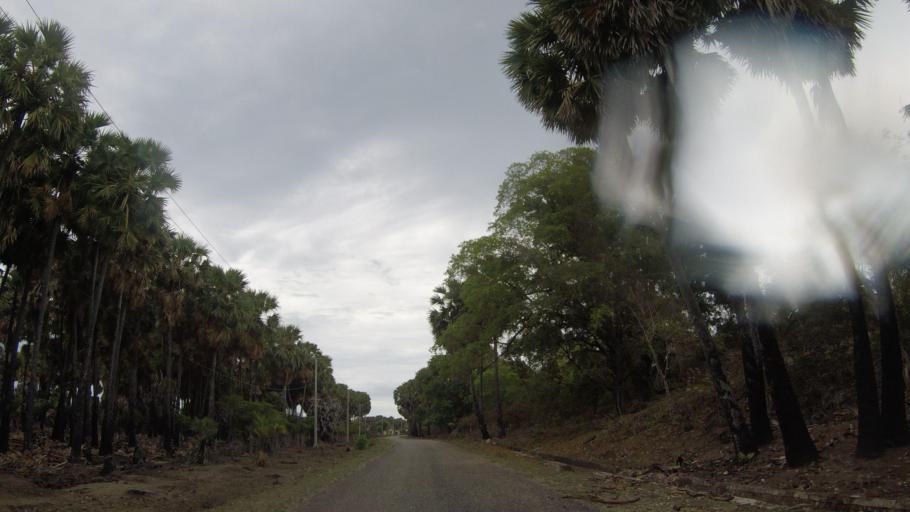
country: TL
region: Lautem
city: Lospalos
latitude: -8.3397
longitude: 126.9347
